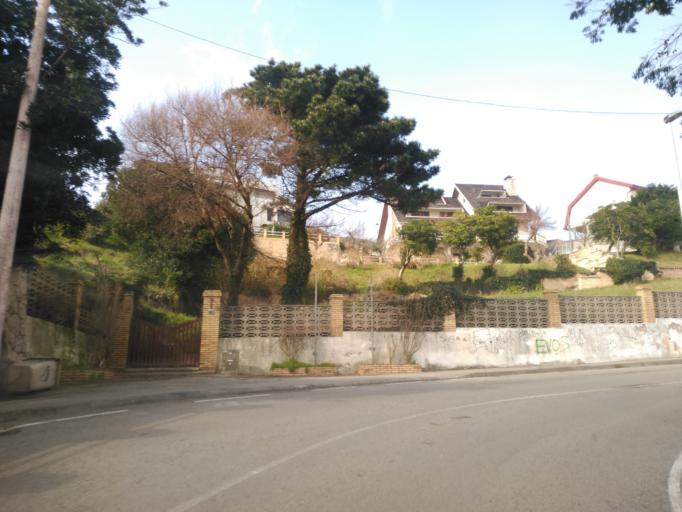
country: ES
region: Cantabria
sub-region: Provincia de Cantabria
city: Suances
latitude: 43.4357
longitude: -4.0462
